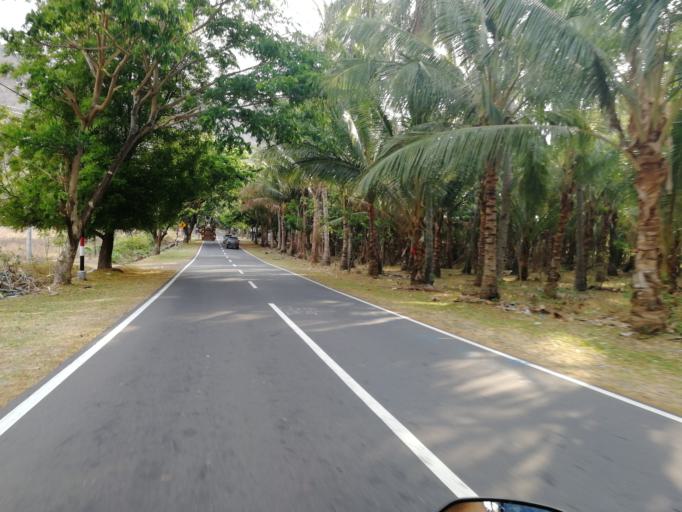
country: ID
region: West Nusa Tenggara
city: Karangsubagan
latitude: -8.4410
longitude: 116.0434
